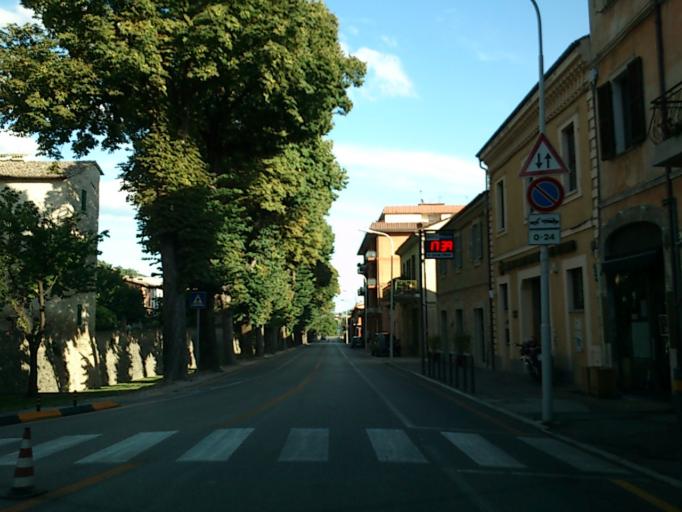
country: IT
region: The Marches
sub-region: Provincia di Pesaro e Urbino
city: Urbania
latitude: 43.6677
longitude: 12.5211
